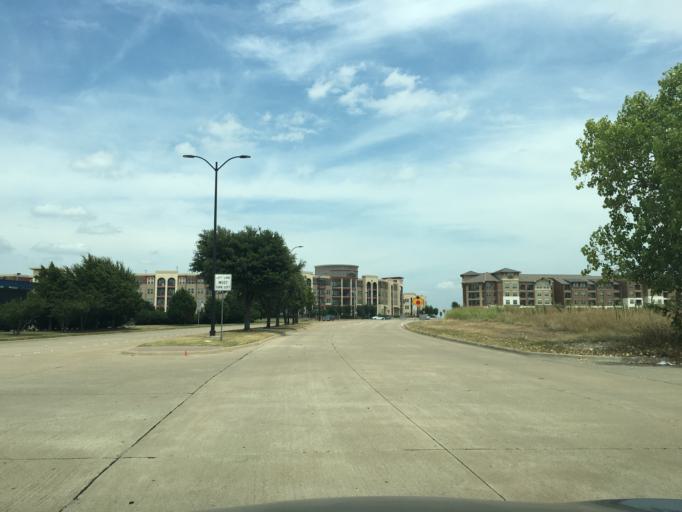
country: US
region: Texas
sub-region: Collin County
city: Frisco
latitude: 33.1051
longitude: -96.8028
